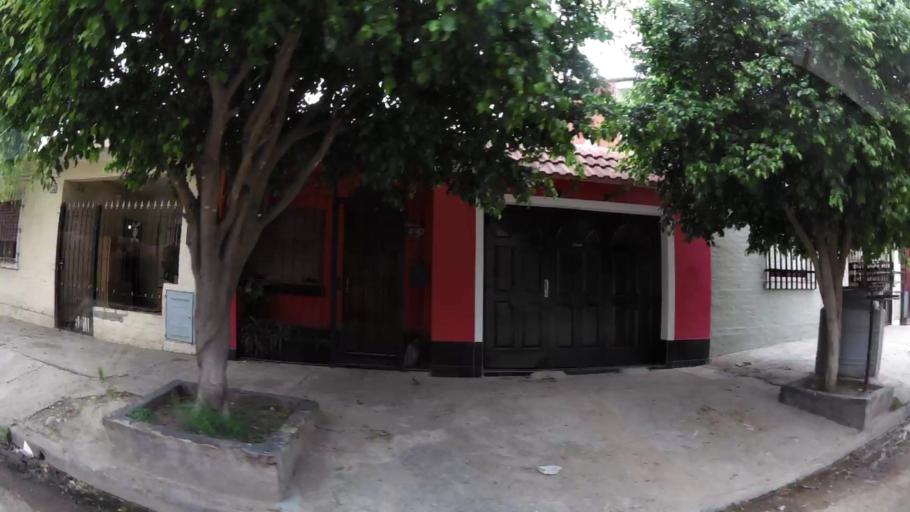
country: AR
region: Buenos Aires
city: San Justo
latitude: -34.6772
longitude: -58.5226
